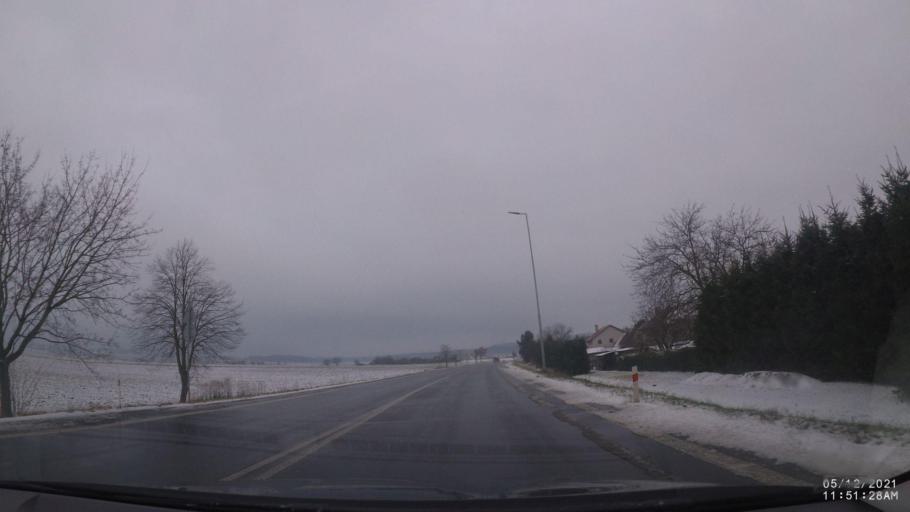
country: CZ
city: Dobruska
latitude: 50.2944
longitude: 16.1685
